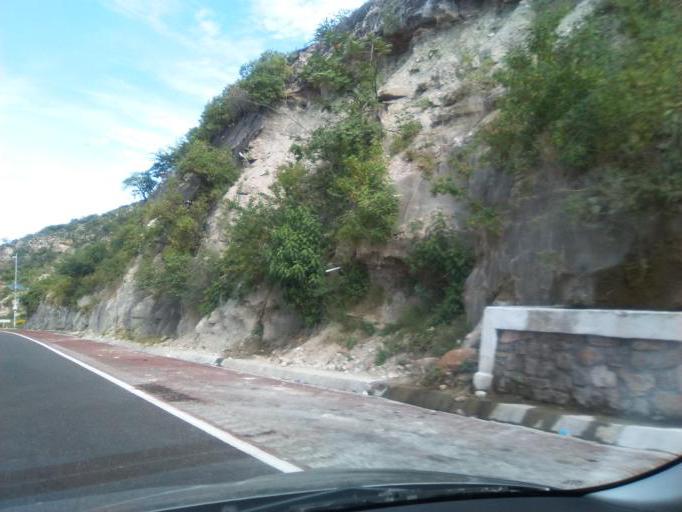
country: MX
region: Guerrero
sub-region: Huitzuco de los Figueroa
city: San Francisco Ozomatlan
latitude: 17.8931
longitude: -99.3913
